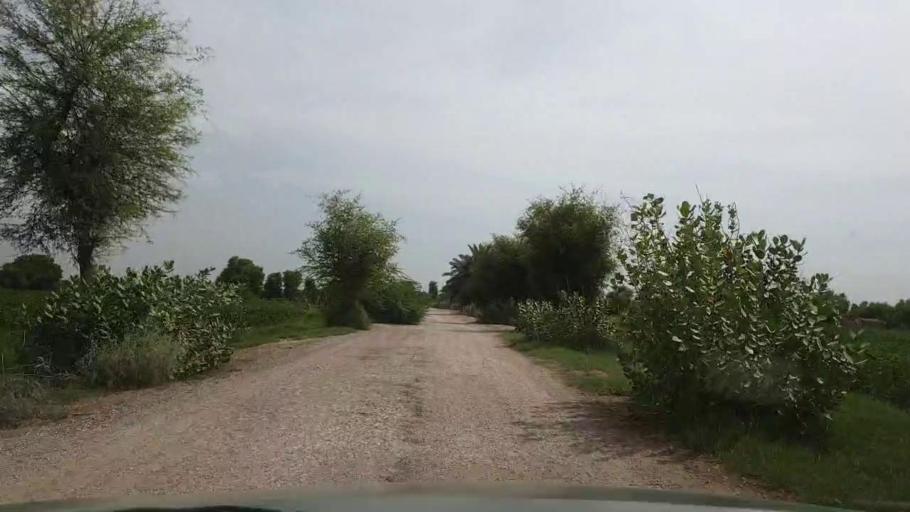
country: PK
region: Sindh
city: Kot Diji
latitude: 27.1178
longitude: 69.0248
